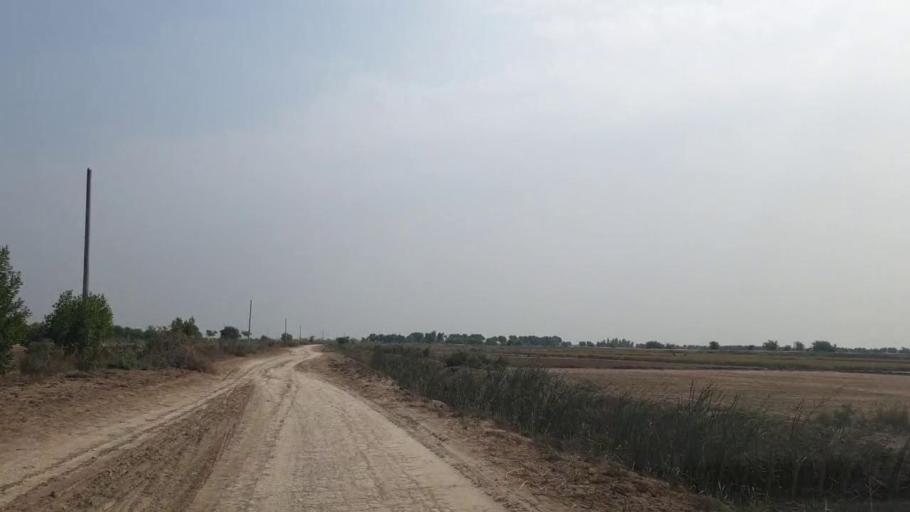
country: PK
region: Sindh
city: Badin
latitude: 24.7632
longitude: 68.7849
